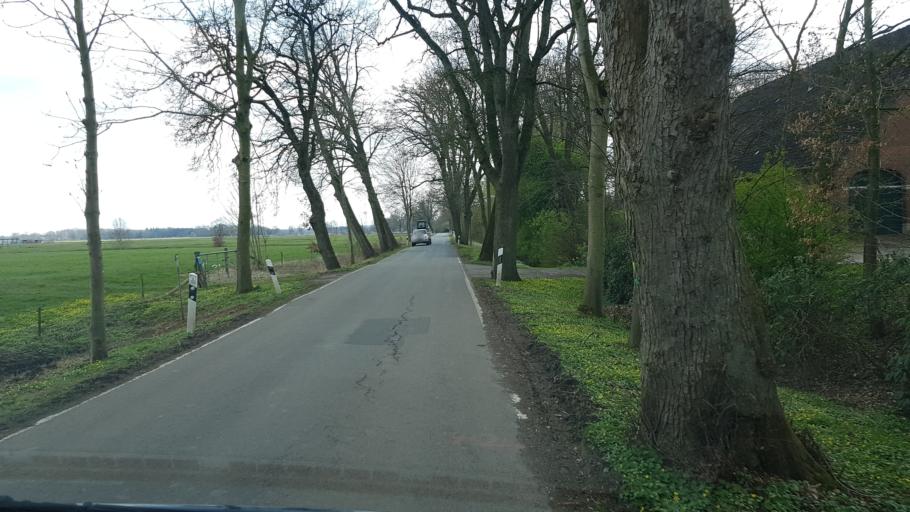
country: DE
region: Lower Saxony
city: Rastede
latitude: 53.2753
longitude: 8.2828
